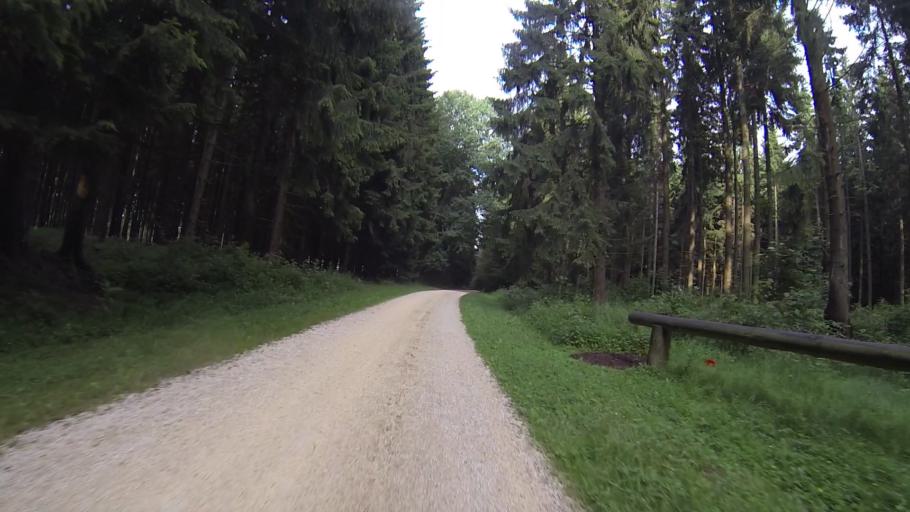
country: DE
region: Baden-Wuerttemberg
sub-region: Regierungsbezirk Stuttgart
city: Neresheim
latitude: 48.7253
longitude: 10.2881
